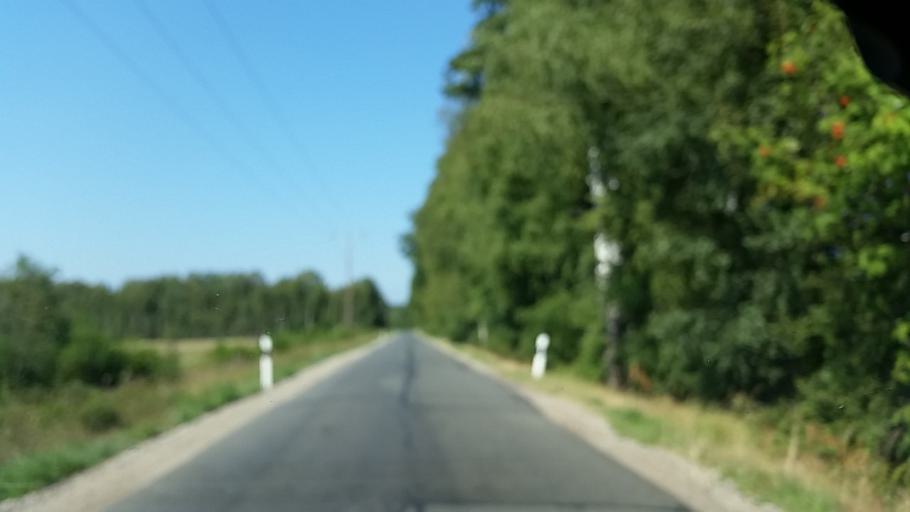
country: DE
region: Lower Saxony
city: Schoneworde
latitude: 52.5984
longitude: 10.6581
